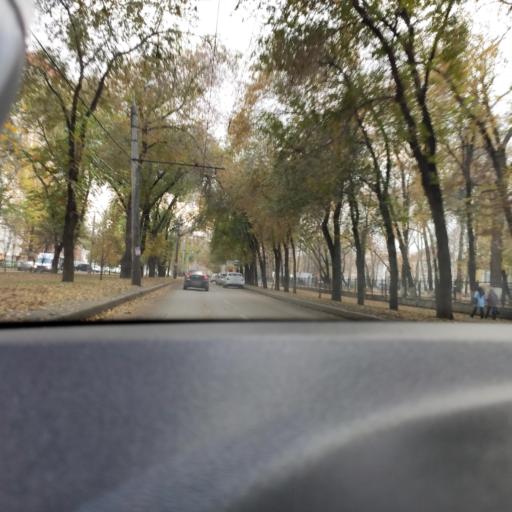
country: RU
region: Samara
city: Samara
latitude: 53.2199
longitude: 50.2444
